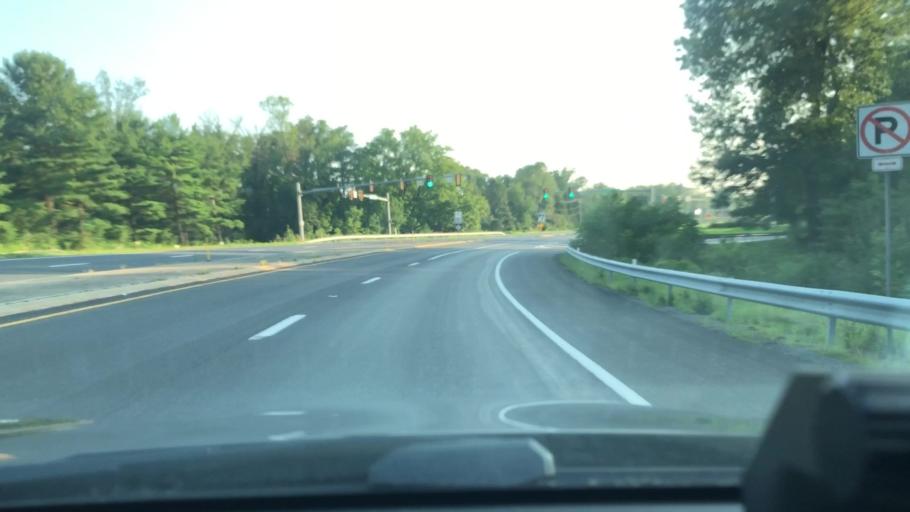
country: US
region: Pennsylvania
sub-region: Lehigh County
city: Coopersburg
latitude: 40.5513
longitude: -75.4202
